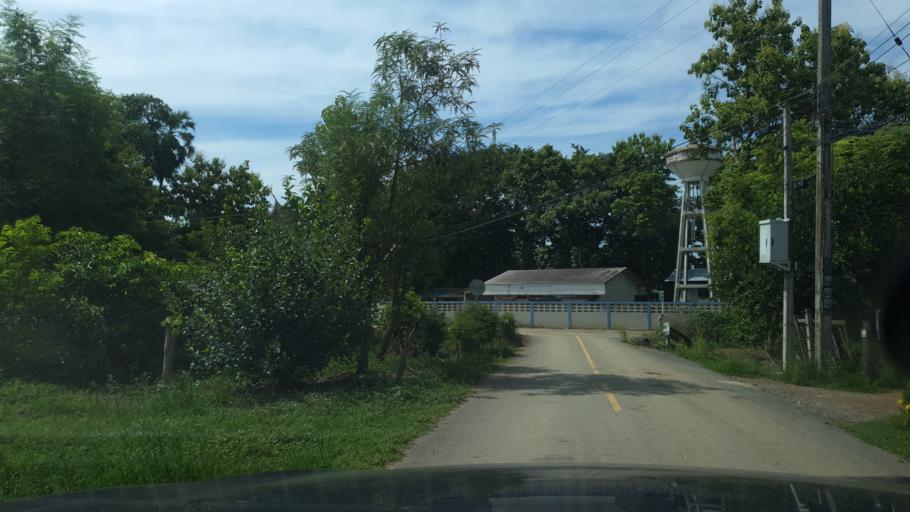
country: TH
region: Sukhothai
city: Sawankhalok
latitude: 17.2159
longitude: 99.7184
